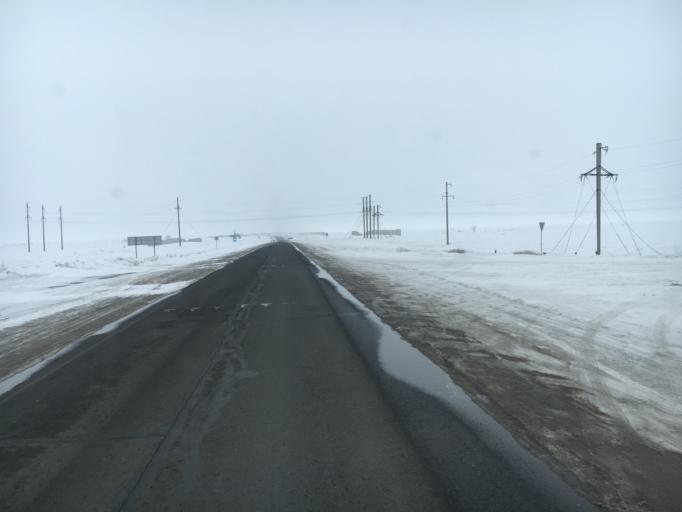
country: KZ
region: Batys Qazaqstan
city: Fedorovka
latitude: 50.7621
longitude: 51.9119
